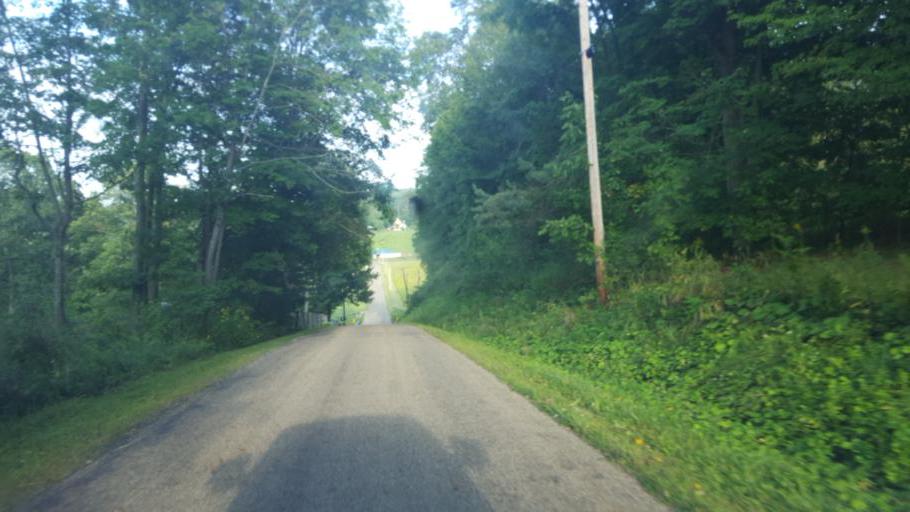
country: US
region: Ohio
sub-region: Sandusky County
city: Bellville
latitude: 40.6597
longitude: -82.4897
